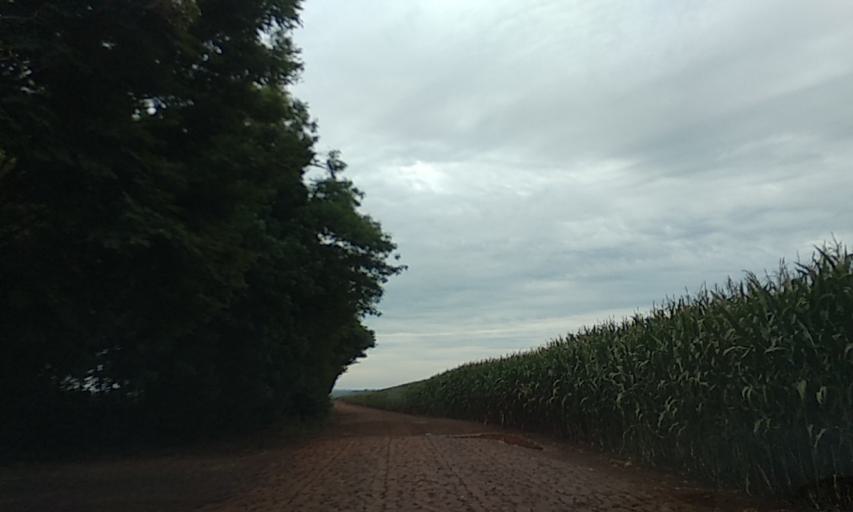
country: BR
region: Parana
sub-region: Marechal Candido Rondon
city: Marechal Candido Rondon
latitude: -24.5409
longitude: -54.0949
